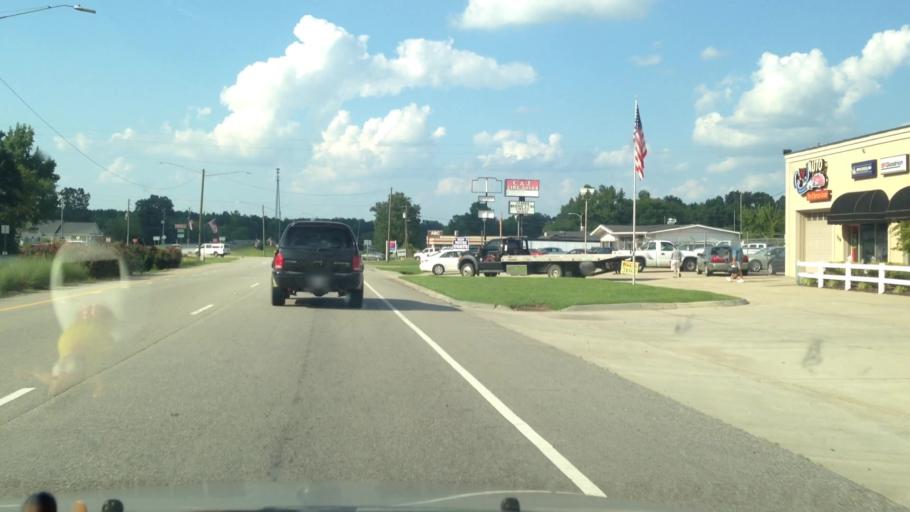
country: US
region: North Carolina
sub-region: Harnett County
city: Lillington
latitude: 35.4026
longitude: -78.8147
